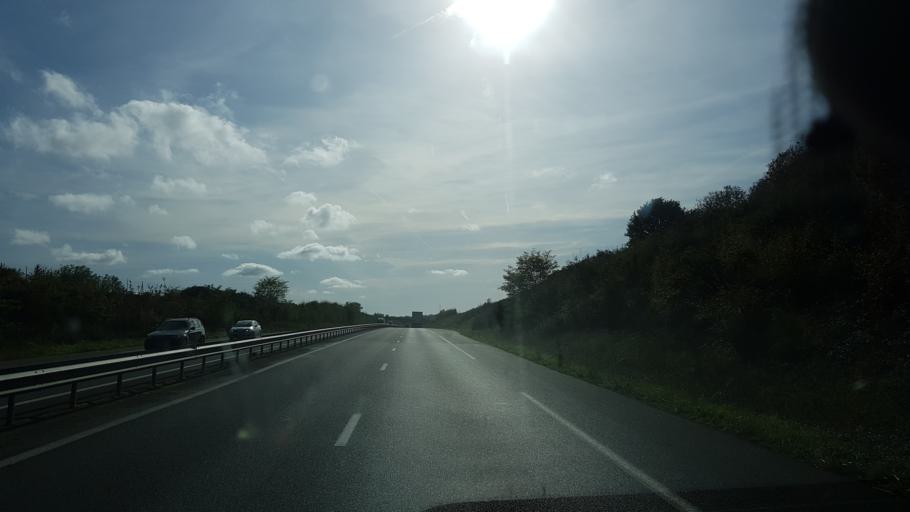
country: FR
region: Poitou-Charentes
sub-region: Departement de la Charente
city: Taponnat-Fleurignac
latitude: 45.7679
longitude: 0.3986
